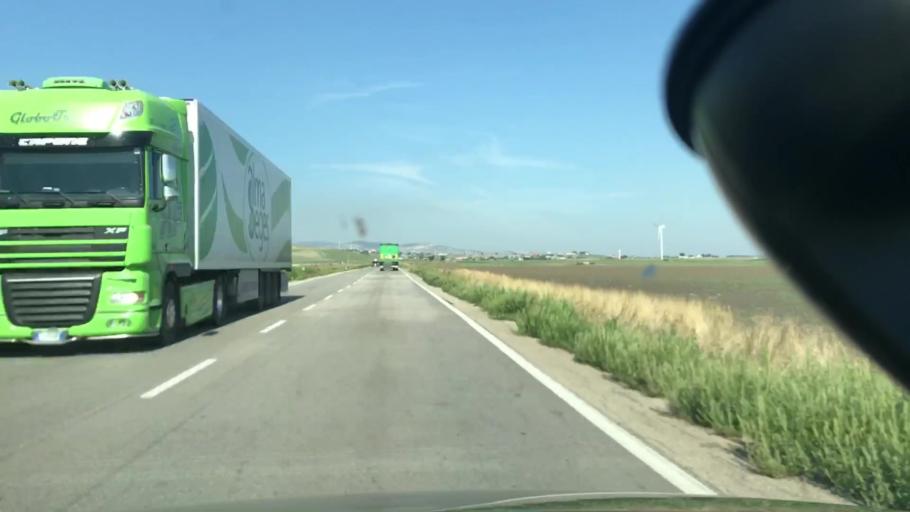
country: IT
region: Apulia
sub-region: Provincia di Foggia
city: Candela
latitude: 41.1300
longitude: 15.5555
